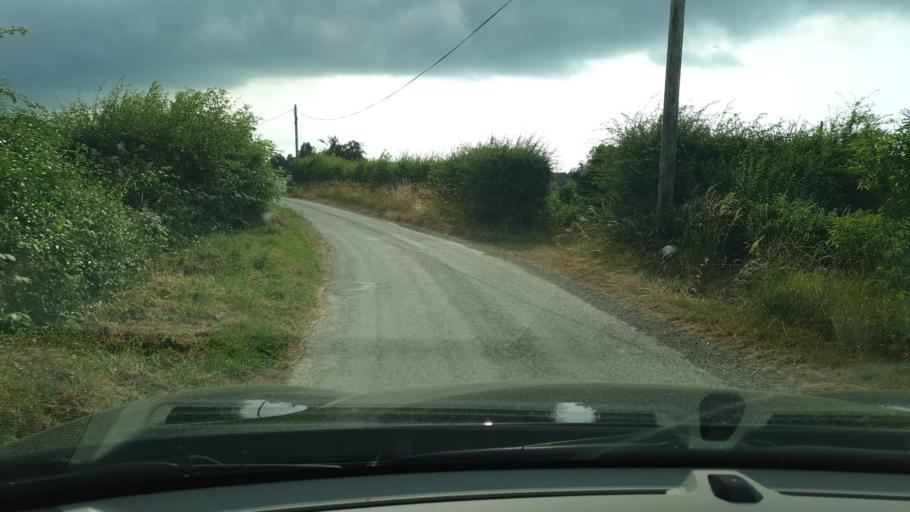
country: IE
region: Leinster
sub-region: An Mhi
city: Ratoath
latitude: 53.4707
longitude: -6.4553
